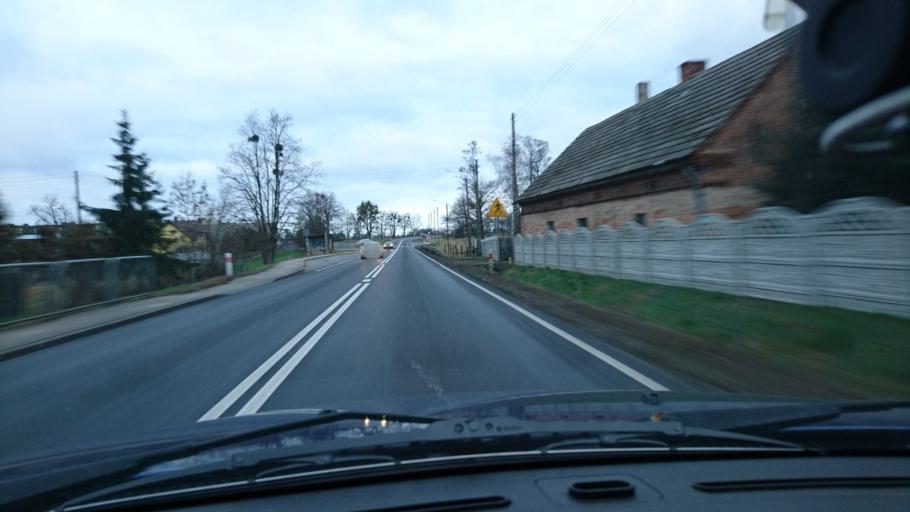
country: PL
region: Opole Voivodeship
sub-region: Powiat kluczborski
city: Byczyna
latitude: 51.0817
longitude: 18.1990
